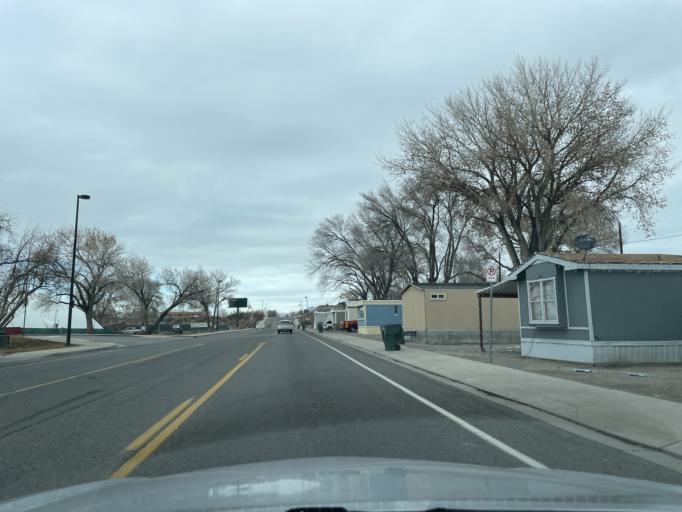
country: US
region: Colorado
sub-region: Mesa County
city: Grand Junction
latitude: 39.0821
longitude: -108.5801
